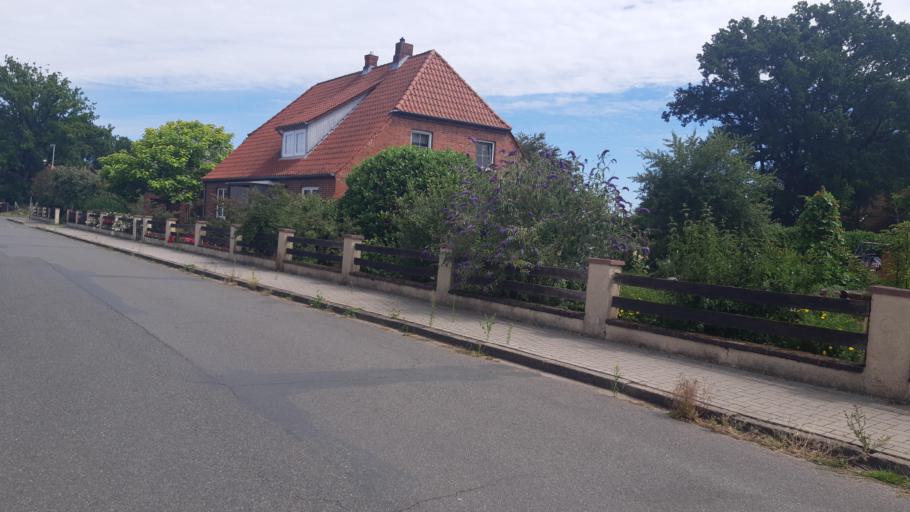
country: DE
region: Lower Saxony
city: Tosterglope
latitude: 53.2377
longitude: 10.7807
